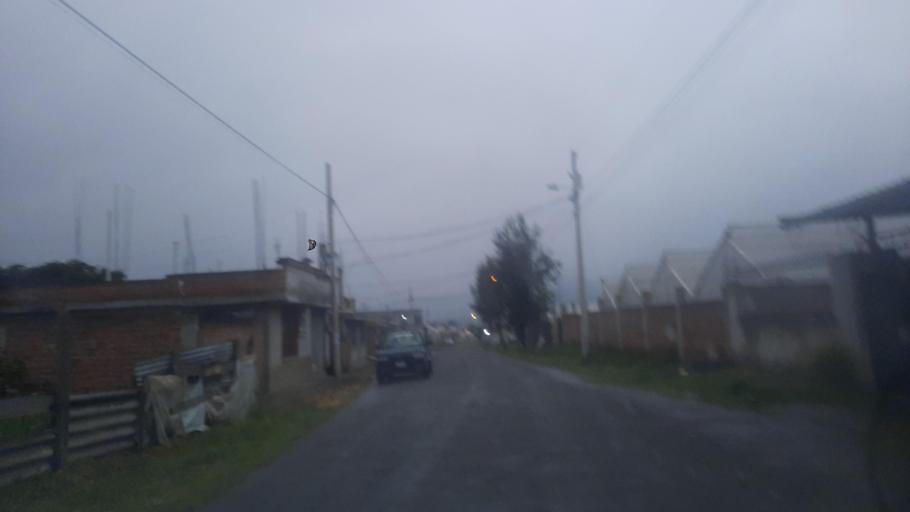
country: EC
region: Chimborazo
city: Riobamba
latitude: -1.6885
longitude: -78.6694
